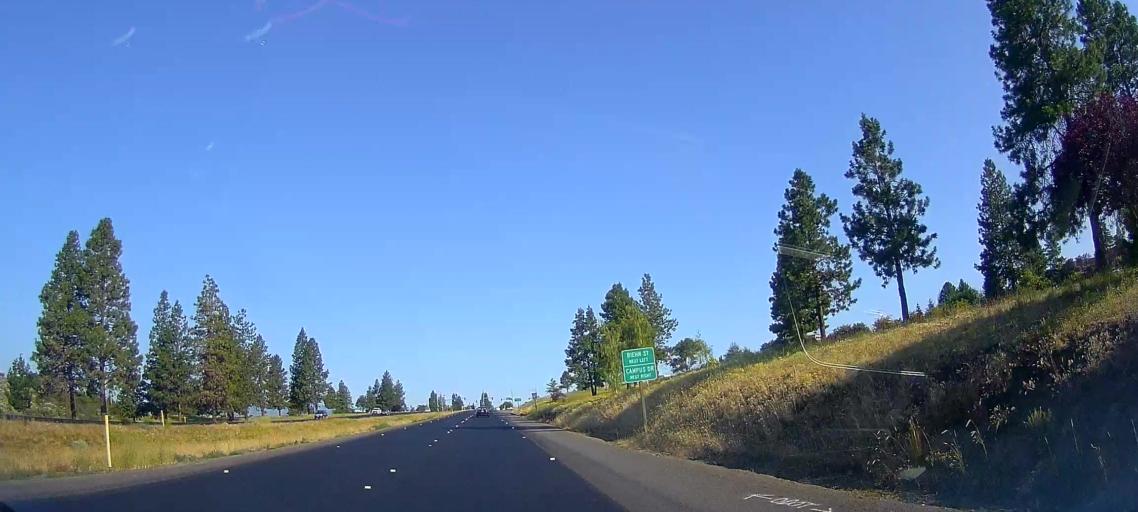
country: US
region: Oregon
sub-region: Klamath County
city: Klamath Falls
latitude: 42.2464
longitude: -121.7878
